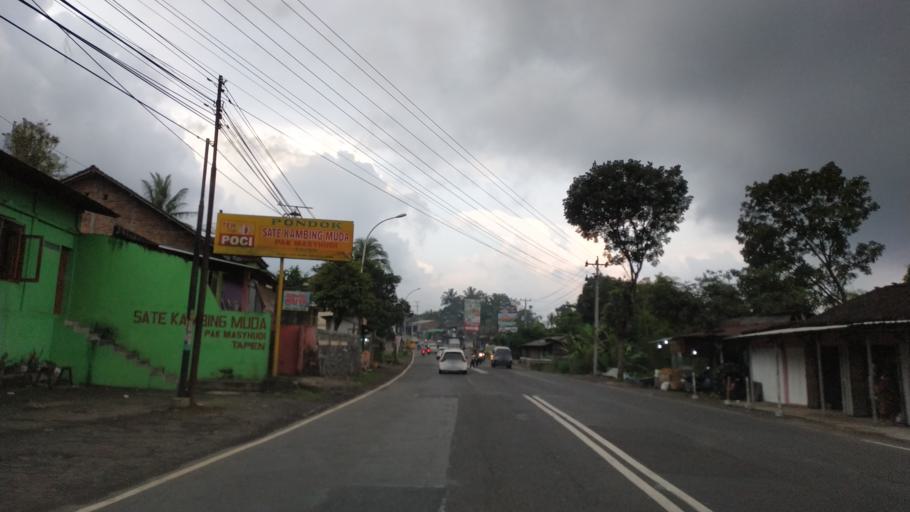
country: ID
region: Central Java
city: Salatiga
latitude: -7.2926
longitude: 110.4679
